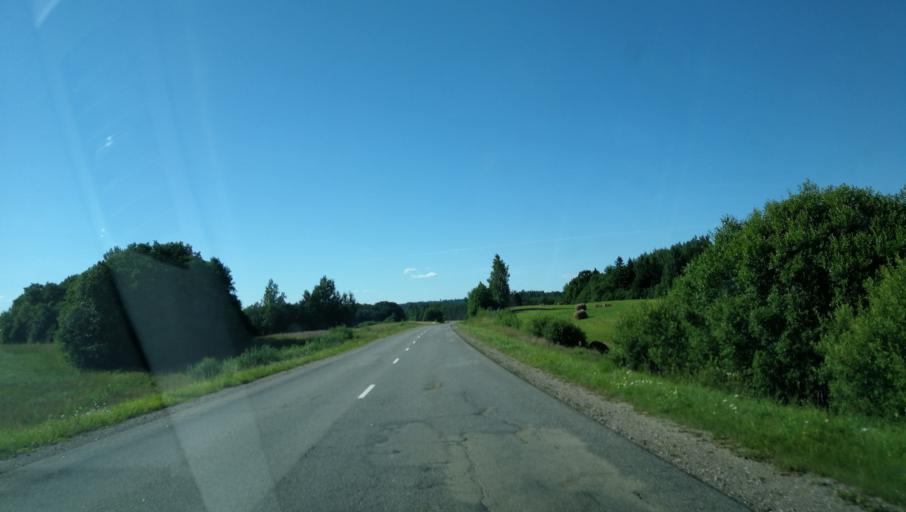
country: LV
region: Jaunpiebalga
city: Jaunpiebalga
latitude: 56.9874
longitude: 26.0170
